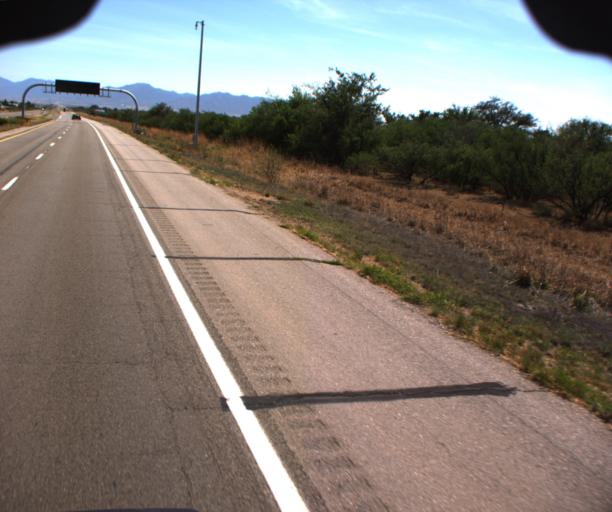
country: US
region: Arizona
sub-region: Cochise County
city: Huachuca City
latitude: 31.7225
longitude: -110.3504
